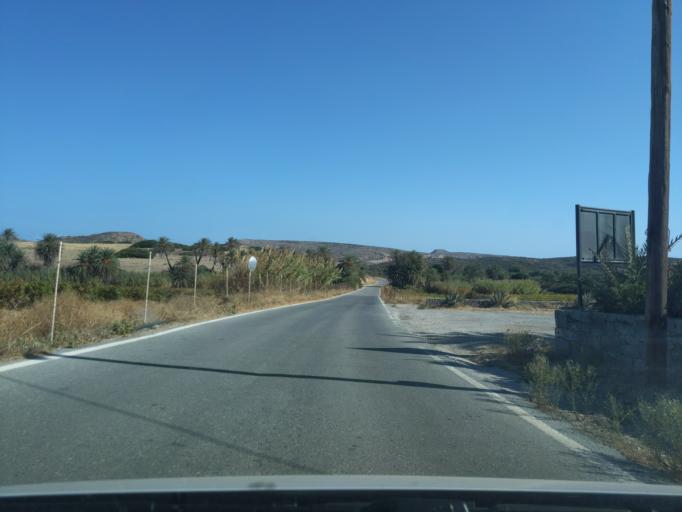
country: GR
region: Crete
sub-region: Nomos Lasithiou
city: Palekastro
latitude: 35.2503
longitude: 26.2512
